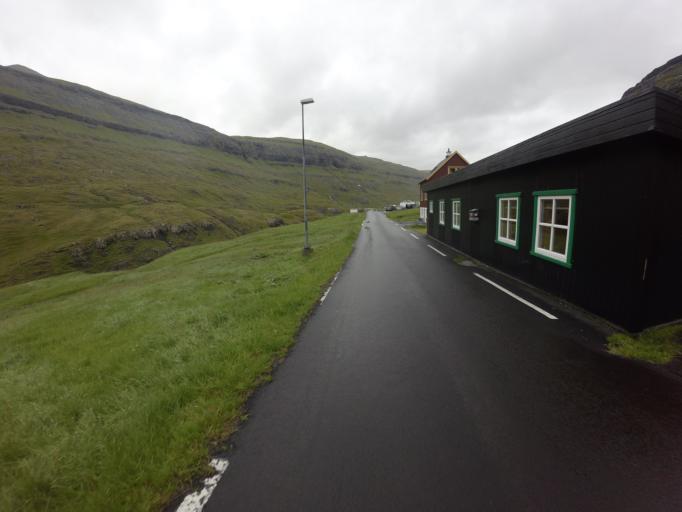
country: FO
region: Streymoy
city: Vestmanna
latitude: 62.2428
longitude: -7.1709
